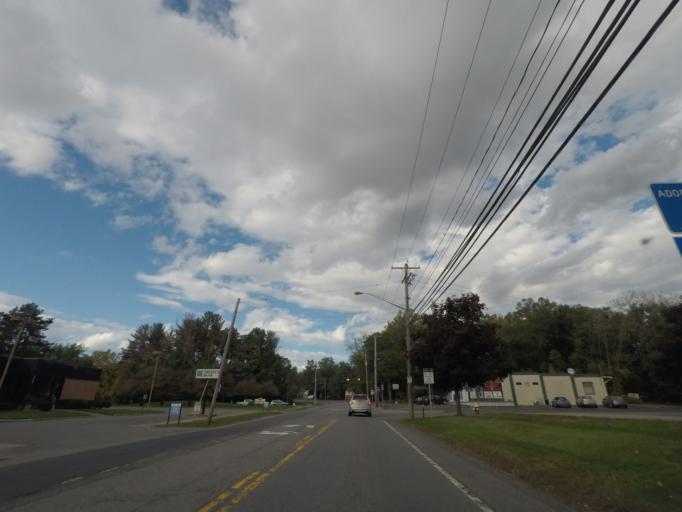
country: US
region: New York
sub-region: Albany County
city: Voorheesville
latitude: 42.7157
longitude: -73.9321
